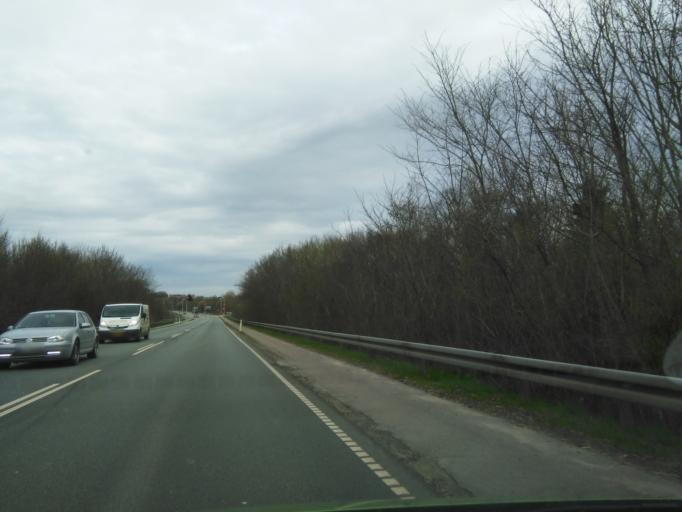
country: DK
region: Central Jutland
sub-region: Skanderborg Kommune
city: Stilling
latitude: 56.0612
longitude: 9.9788
